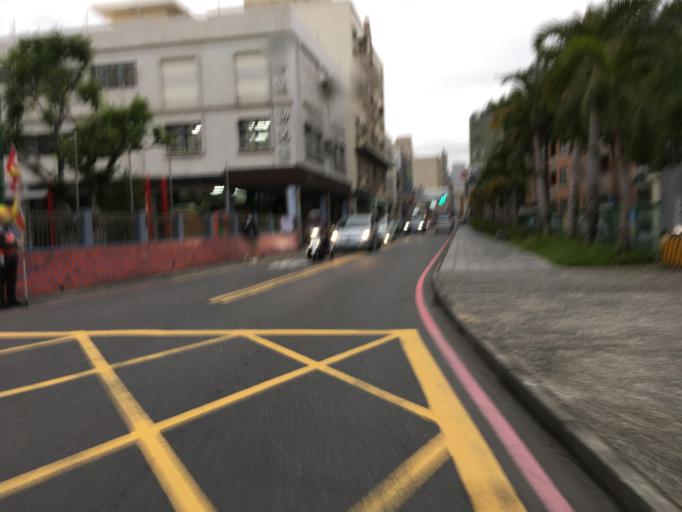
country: TW
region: Taiwan
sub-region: Yilan
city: Yilan
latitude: 24.6776
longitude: 121.7611
